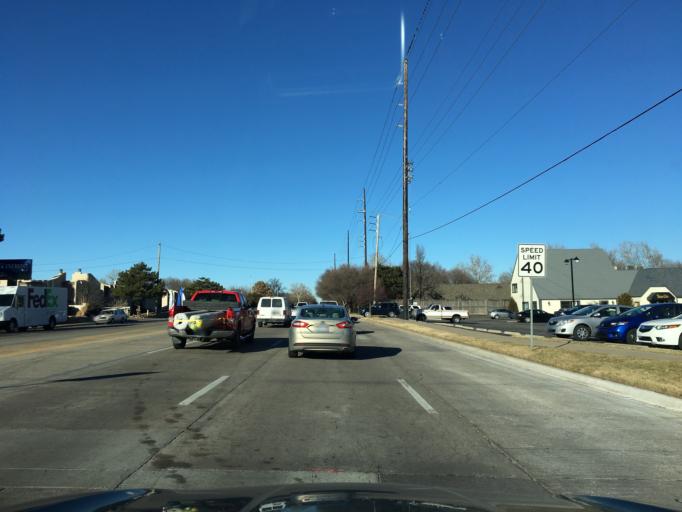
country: US
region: Kansas
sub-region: Sedgwick County
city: Bellaire
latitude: 37.6945
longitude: -97.2445
